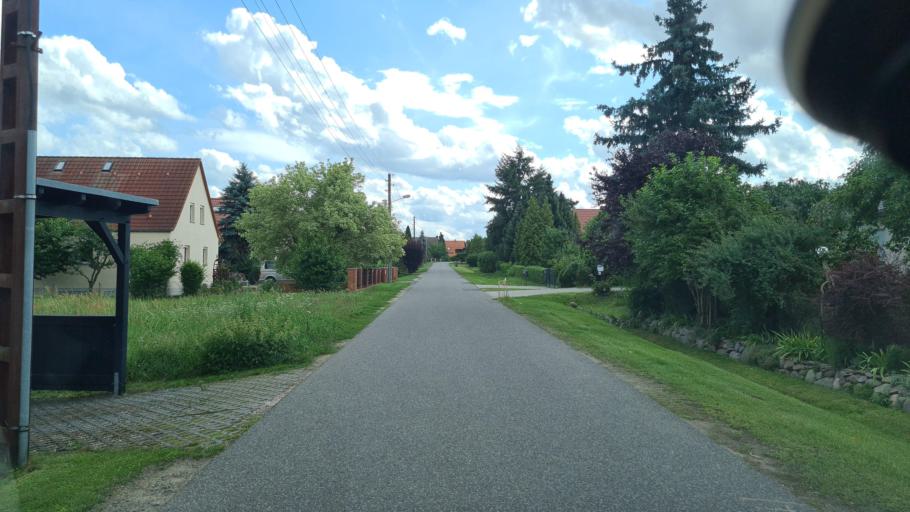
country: DE
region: Brandenburg
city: Drebkau
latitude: 51.6359
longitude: 14.2828
